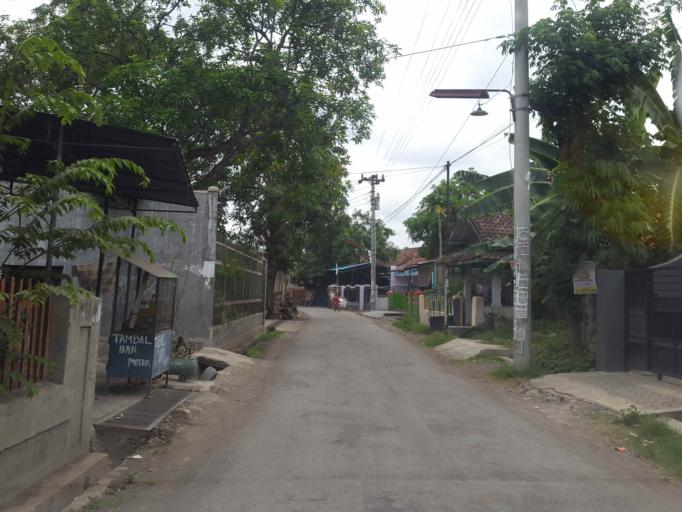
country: ID
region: Central Java
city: Tegal
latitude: -6.9002
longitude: 109.1311
